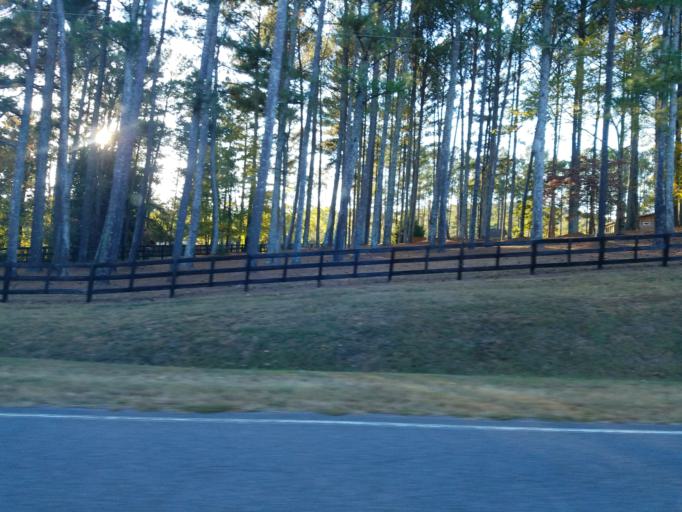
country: US
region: Georgia
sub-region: Bartow County
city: Adairsville
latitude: 34.3362
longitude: -84.9356
